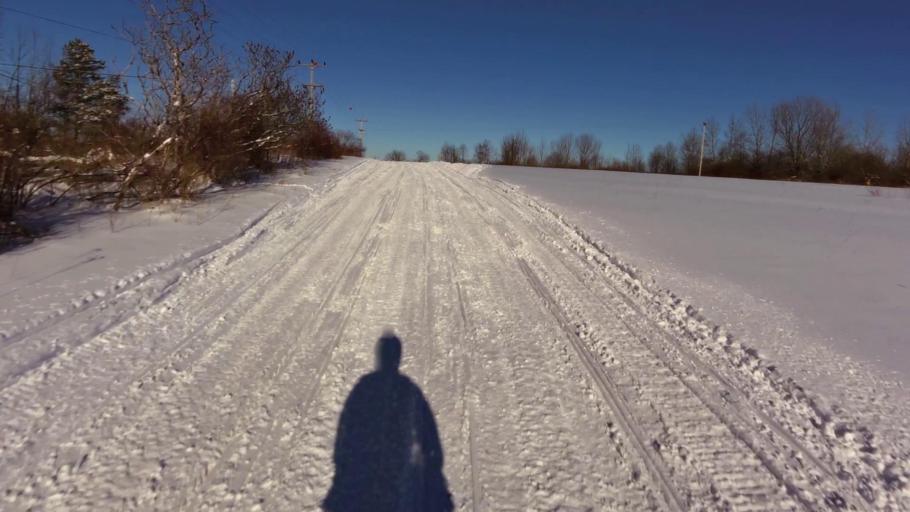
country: US
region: New York
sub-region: Chautauqua County
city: Mayville
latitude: 42.2799
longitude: -79.4434
